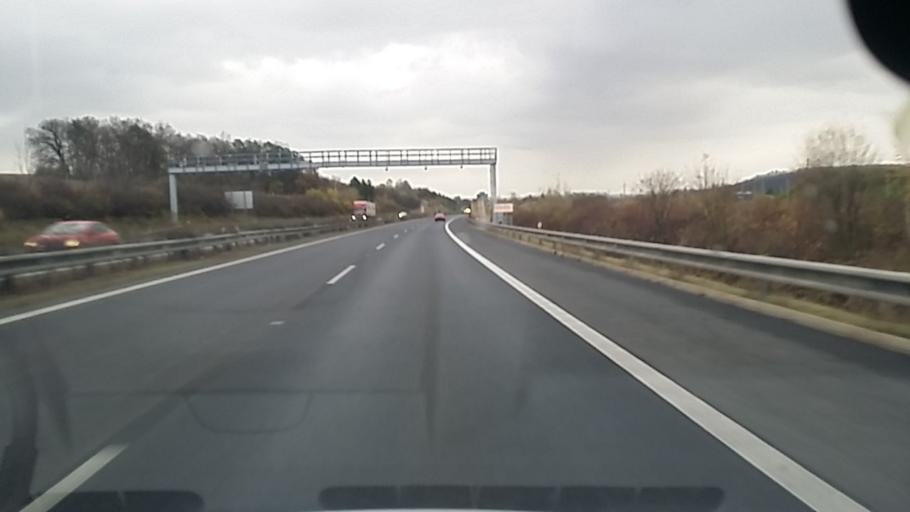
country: CZ
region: Central Bohemia
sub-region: Okres Melnik
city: Veltrusy
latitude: 50.3181
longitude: 14.3105
